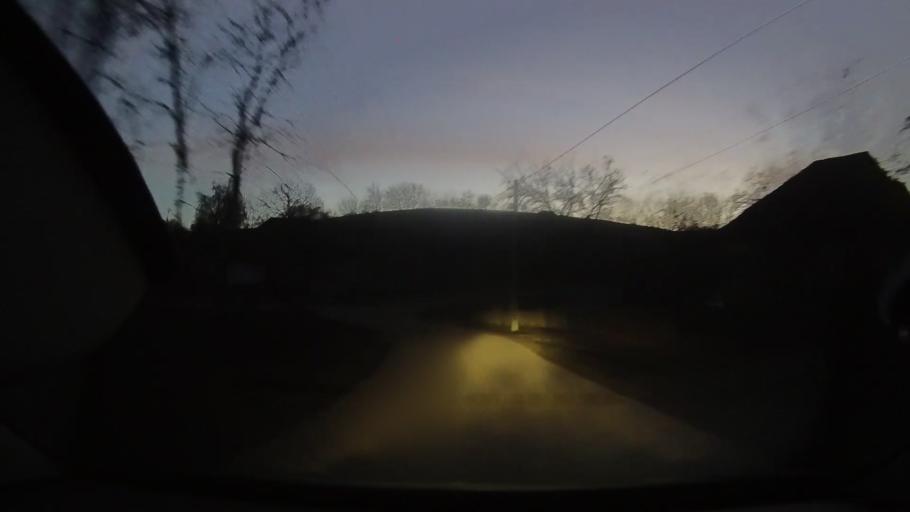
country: RO
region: Bihor
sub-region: Comuna Varciorog
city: Varciorog
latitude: 46.9878
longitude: 22.3287
